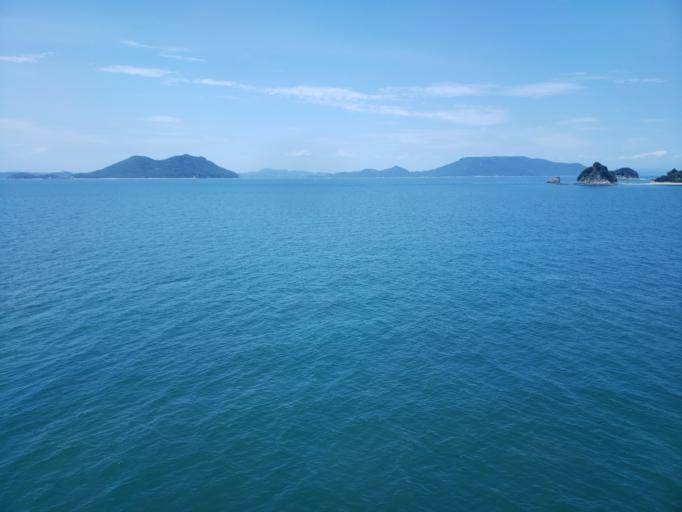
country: JP
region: Kagawa
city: Takamatsu-shi
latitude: 34.3937
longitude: 134.0987
